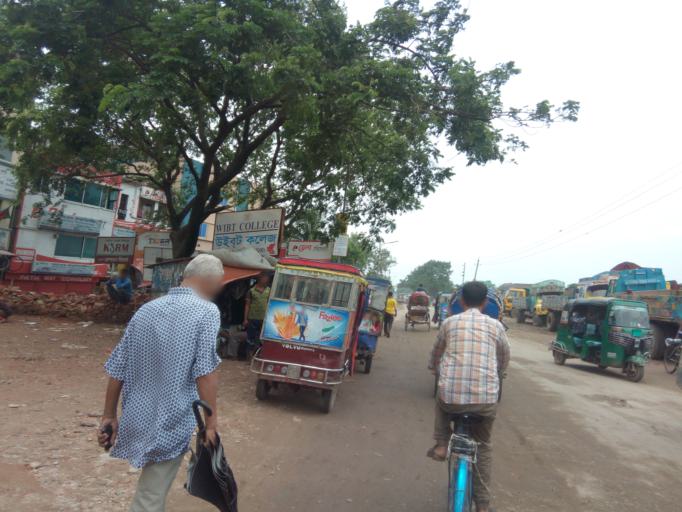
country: BD
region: Dhaka
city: Azimpur
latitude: 23.7552
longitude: 90.3569
